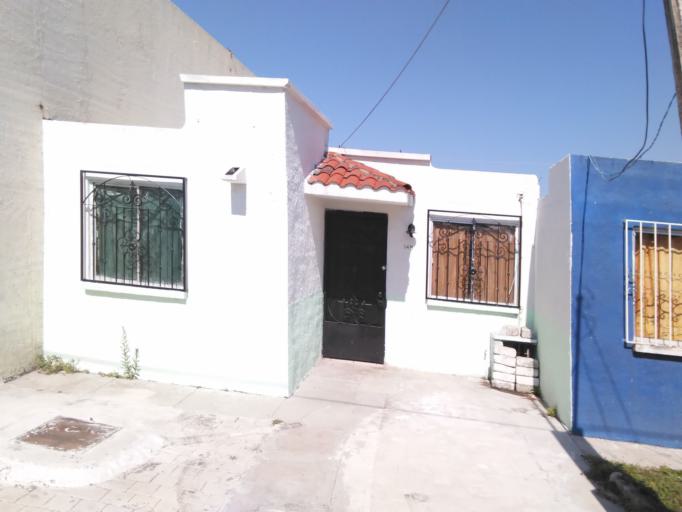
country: MX
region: Nayarit
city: Tepic
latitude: 21.4831
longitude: -104.8523
